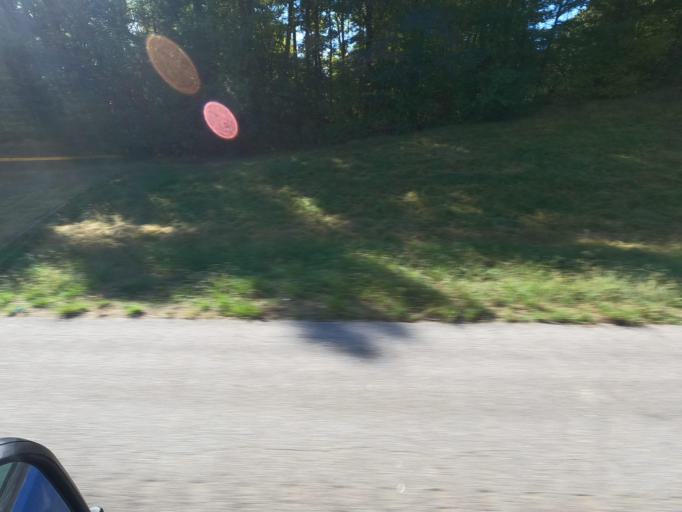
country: US
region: Tennessee
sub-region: Shelby County
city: Arlington
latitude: 35.3086
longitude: -89.7039
